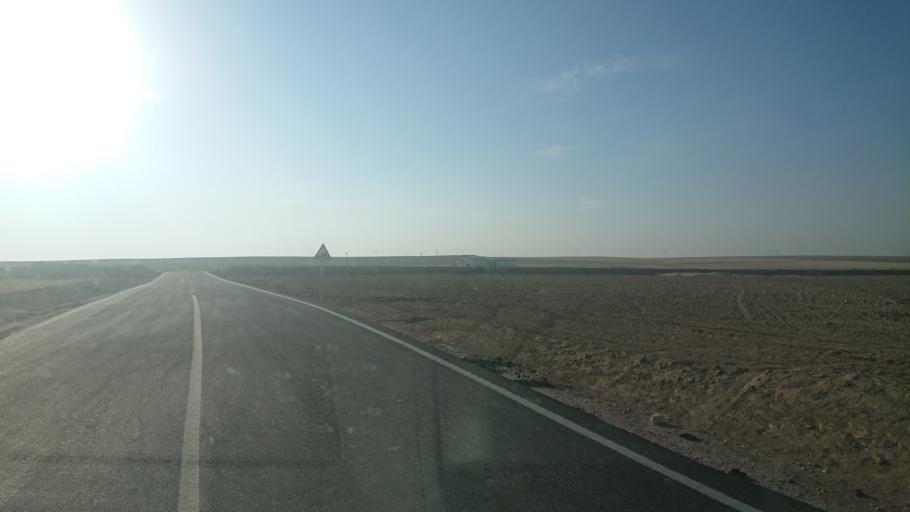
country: TR
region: Aksaray
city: Sultanhani
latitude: 38.0895
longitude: 33.6113
